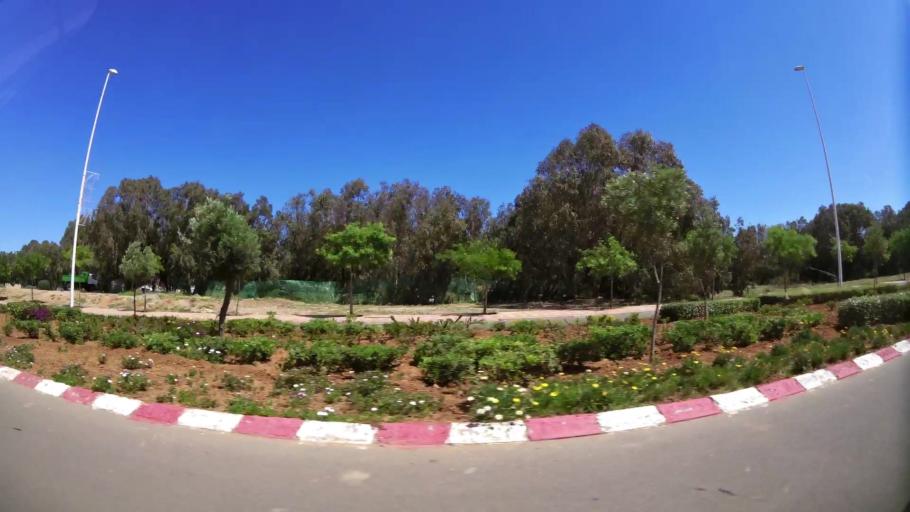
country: MA
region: Oriental
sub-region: Berkane-Taourirt
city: Madagh
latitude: 35.1000
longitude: -2.2860
